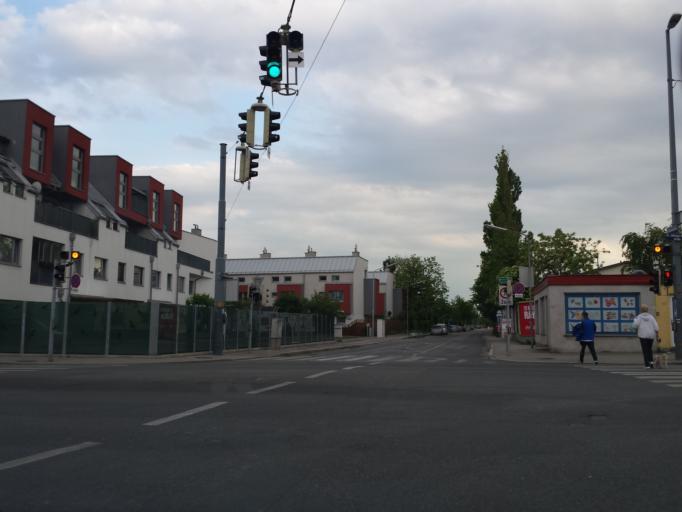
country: AT
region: Lower Austria
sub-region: Politischer Bezirk Ganserndorf
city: Gross-Enzersdorf
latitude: 48.2146
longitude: 16.5196
